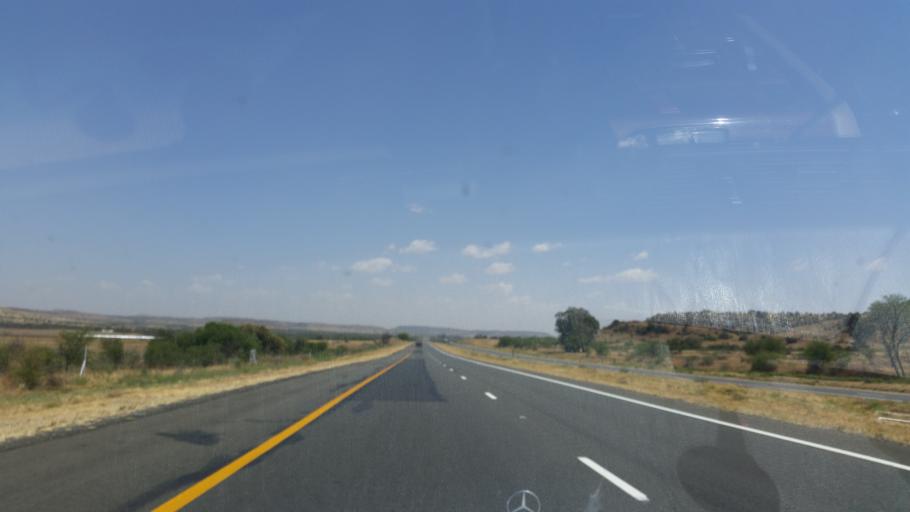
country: ZA
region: Orange Free State
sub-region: Mangaung Metropolitan Municipality
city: Bloemfontein
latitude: -28.9543
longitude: 26.3875
